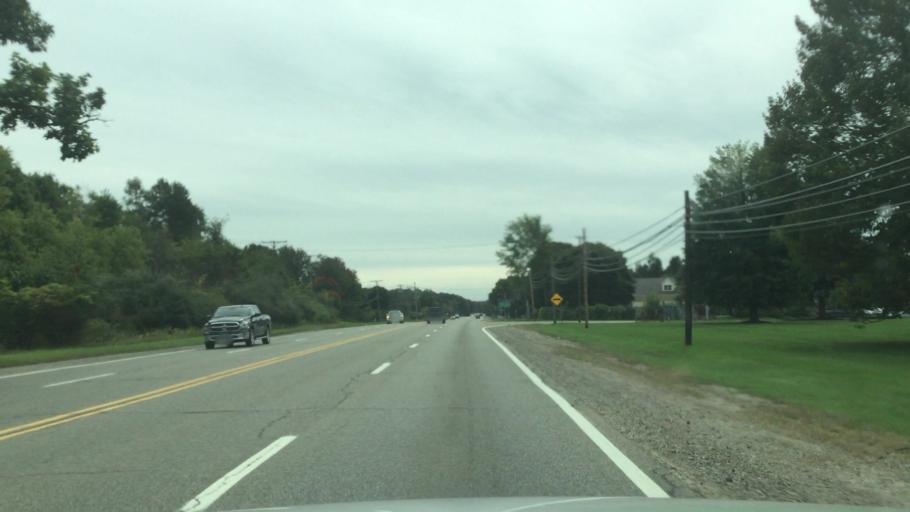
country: US
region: Michigan
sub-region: Oakland County
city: Clarkston
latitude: 42.7759
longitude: -83.4947
